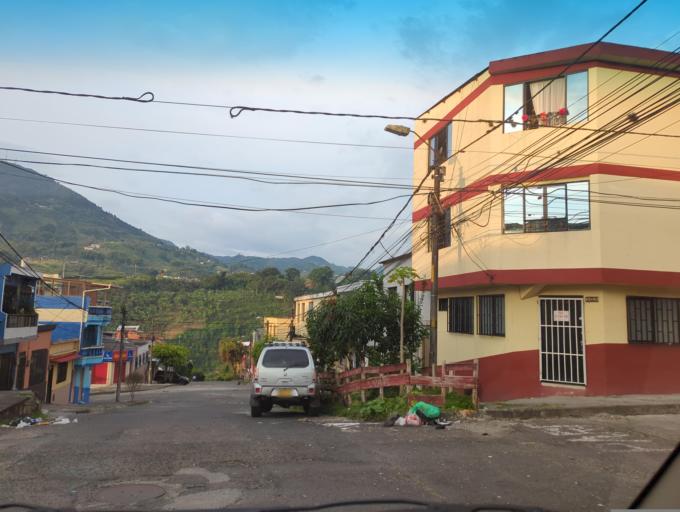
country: CO
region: Risaralda
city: Pereira
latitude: 4.8184
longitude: -75.7082
